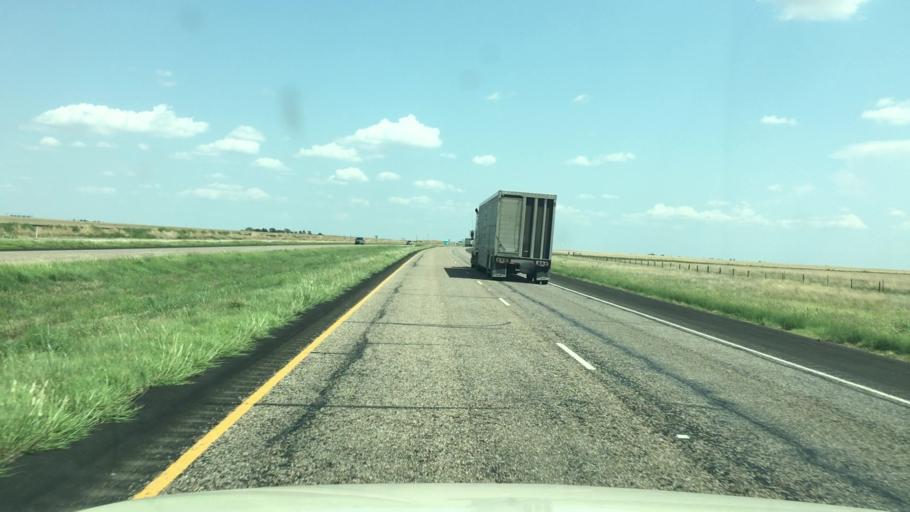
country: US
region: Texas
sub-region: Armstrong County
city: Claude
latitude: 35.1270
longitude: -101.4018
